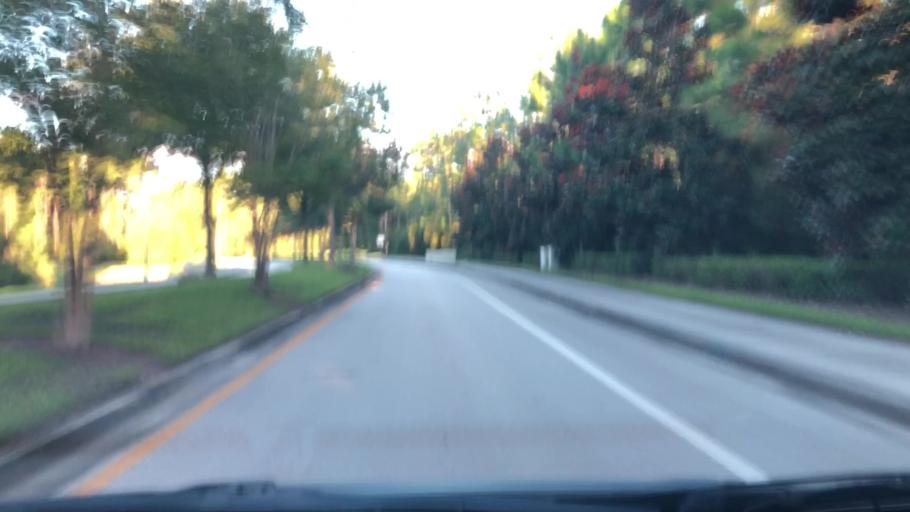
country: US
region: Florida
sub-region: Saint Johns County
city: Palm Valley
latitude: 30.1248
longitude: -81.4304
